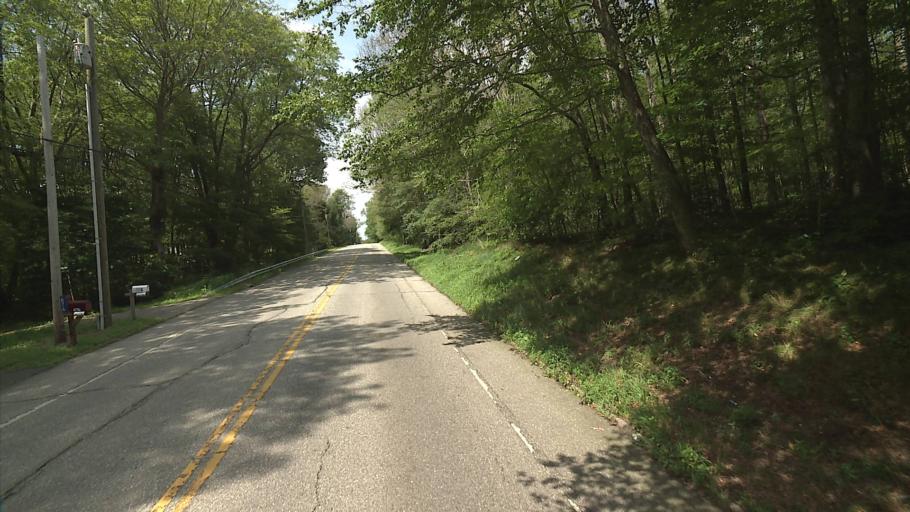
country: US
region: Connecticut
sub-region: New London County
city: Colchester
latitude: 41.5358
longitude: -72.2696
